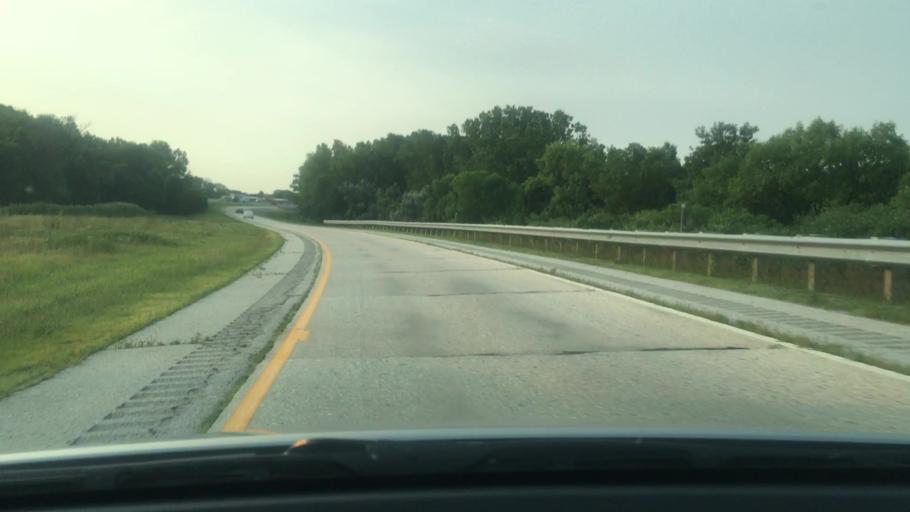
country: US
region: Wisconsin
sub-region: Brown County
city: Ashwaubenon
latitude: 44.4844
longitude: -88.0844
